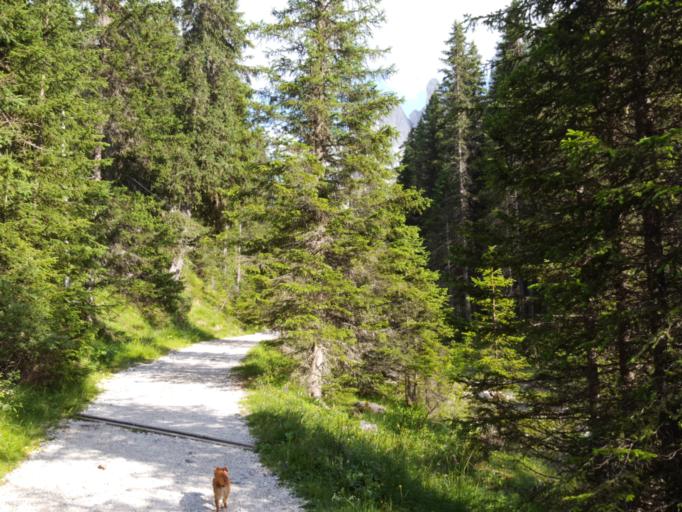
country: IT
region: Trentino-Alto Adige
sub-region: Bolzano
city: Selva
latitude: 46.6330
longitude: 11.7721
